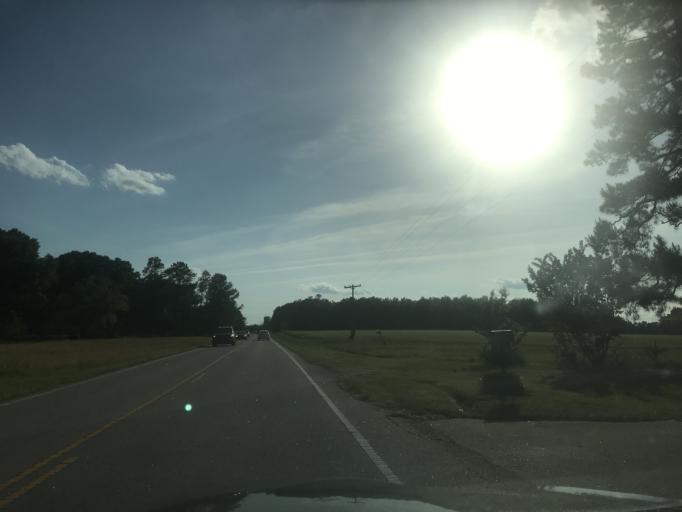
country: US
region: North Carolina
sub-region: Wake County
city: Wendell
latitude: 35.7759
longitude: -78.3956
